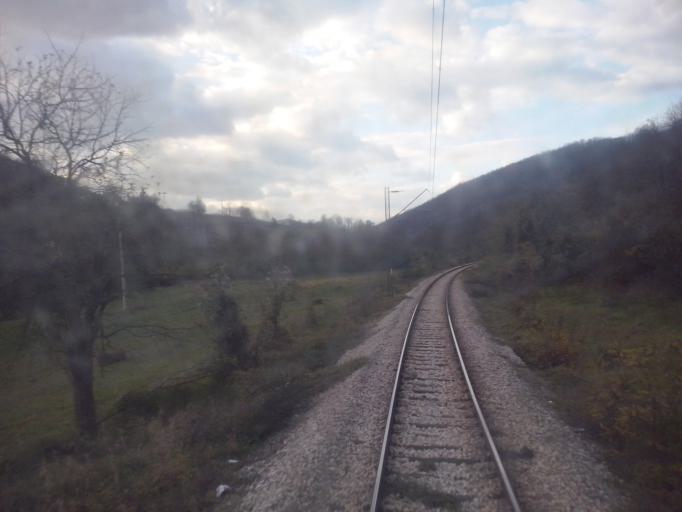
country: RS
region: Central Serbia
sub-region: Zlatiborski Okrug
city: Kosjeric
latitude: 43.9800
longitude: 19.9436
